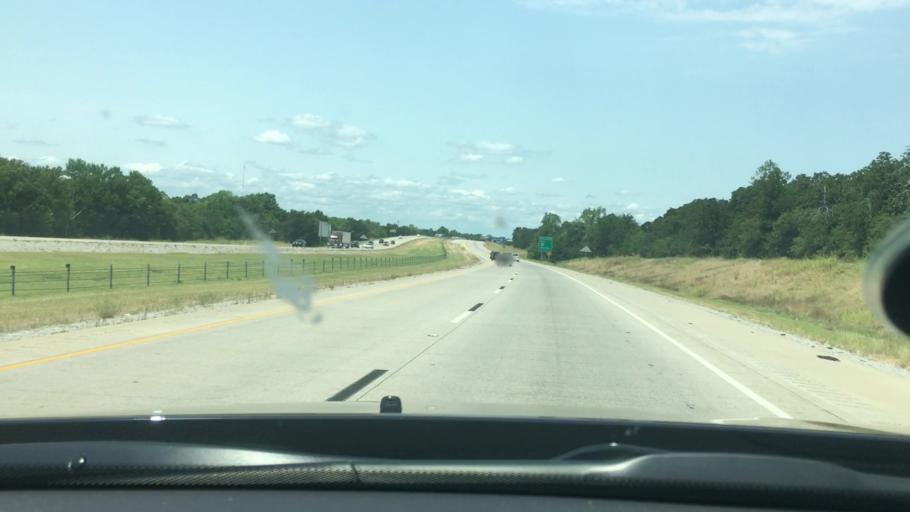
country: US
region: Oklahoma
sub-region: Carter County
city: Ardmore
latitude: 34.1534
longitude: -97.1589
